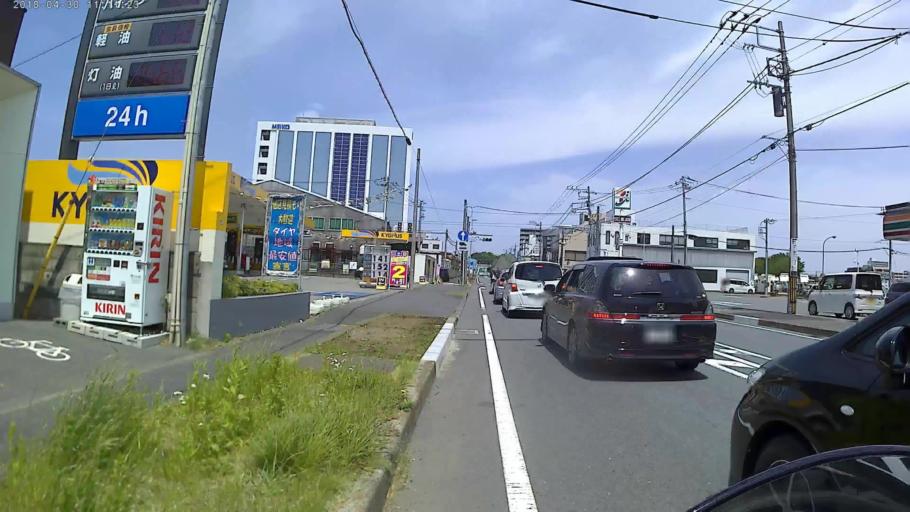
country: JP
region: Kanagawa
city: Minami-rinkan
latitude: 35.4645
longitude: 139.4305
